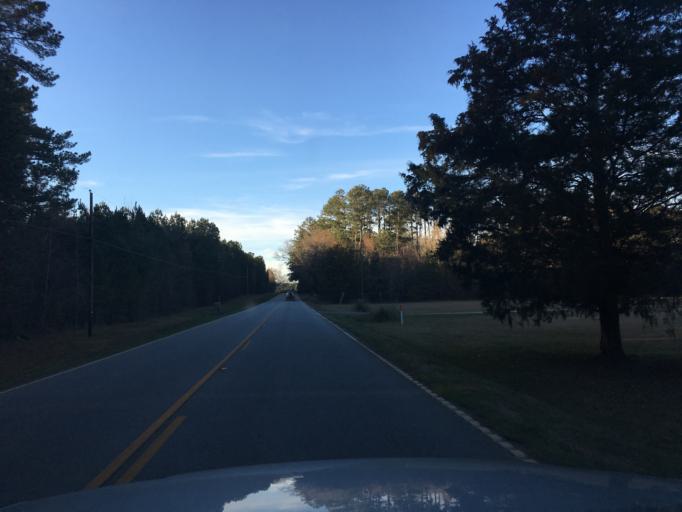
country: US
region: South Carolina
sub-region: Saluda County
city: Saluda
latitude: 34.0793
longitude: -81.8216
